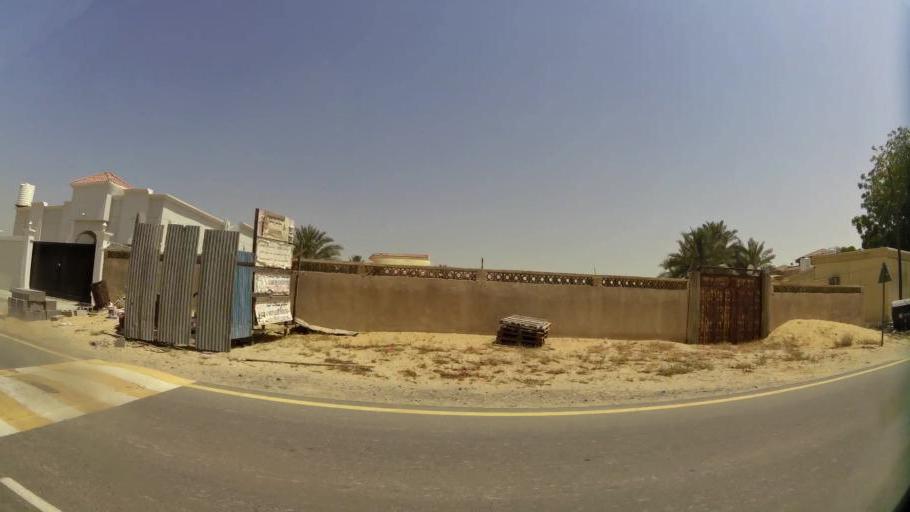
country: AE
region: Ajman
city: Ajman
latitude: 25.4004
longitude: 55.5113
